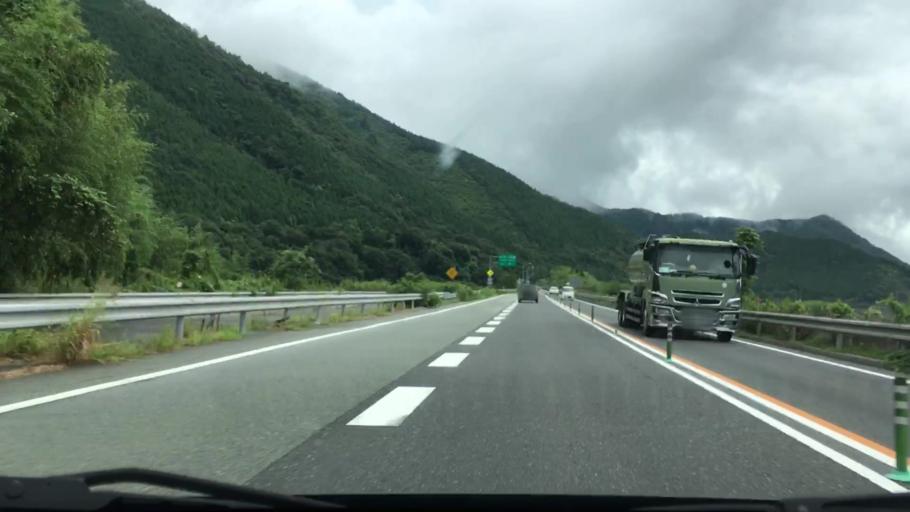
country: JP
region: Hyogo
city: Nishiwaki
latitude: 35.0460
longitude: 134.7660
